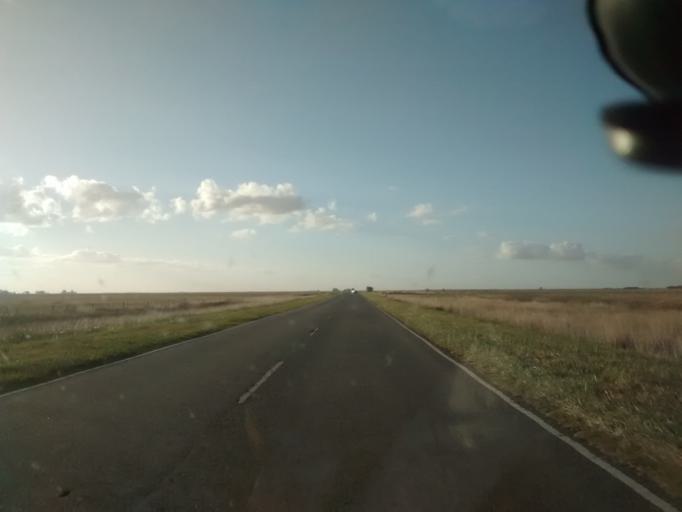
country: AR
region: Buenos Aires
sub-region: Partido de General Belgrano
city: General Belgrano
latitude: -36.0773
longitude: -58.6203
